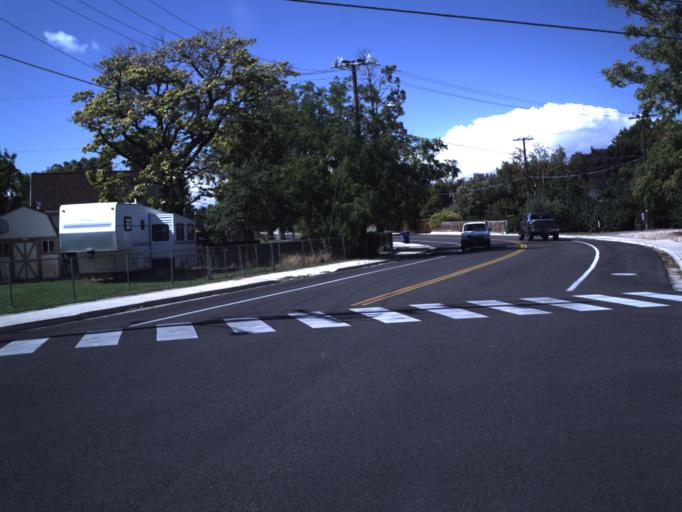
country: US
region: Utah
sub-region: Utah County
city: Spanish Fork
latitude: 40.1151
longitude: -111.6598
